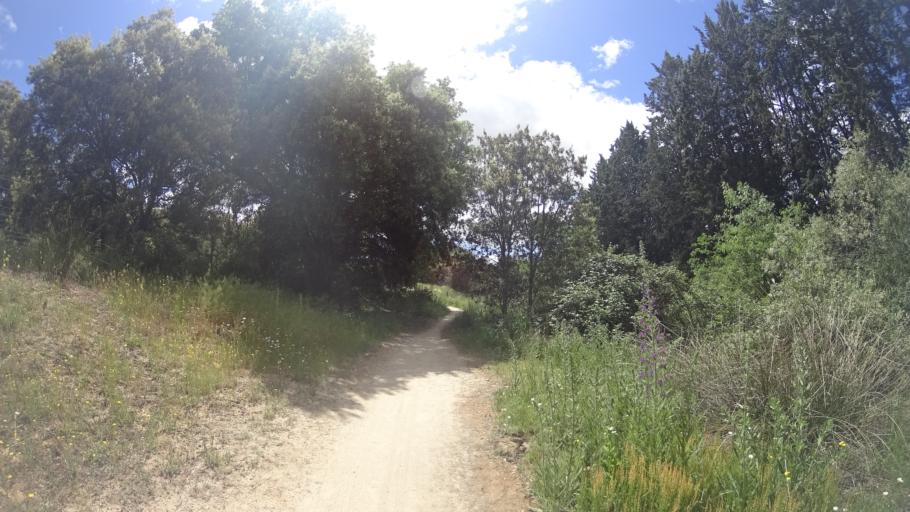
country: ES
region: Madrid
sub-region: Provincia de Madrid
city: Brunete
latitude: 40.3915
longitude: -3.9442
